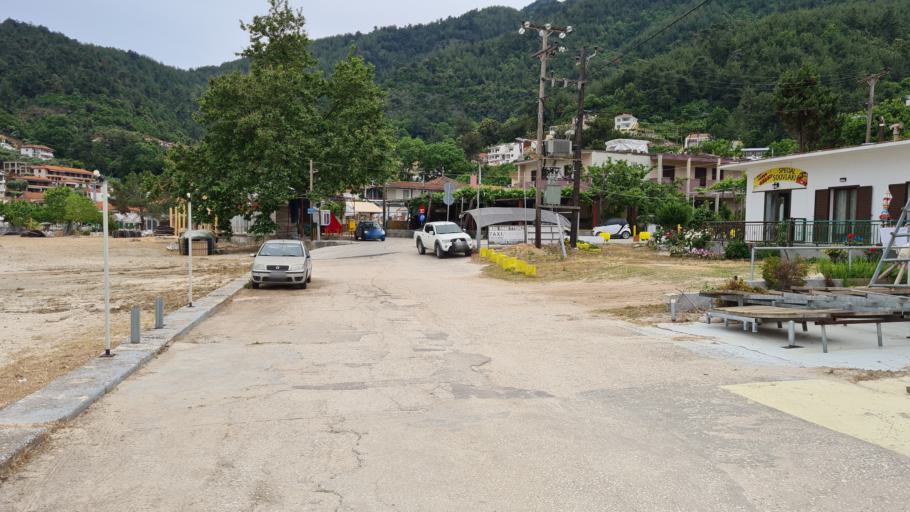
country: GR
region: East Macedonia and Thrace
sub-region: Nomos Kavalas
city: Potamia
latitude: 40.7094
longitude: 24.7597
